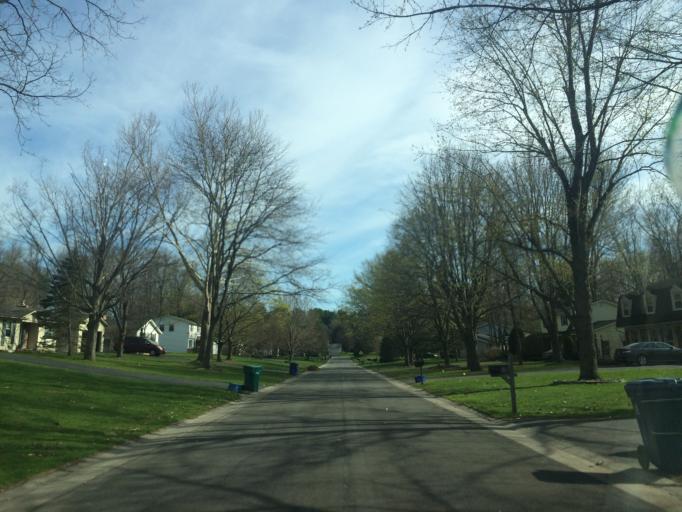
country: US
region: New York
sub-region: Monroe County
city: East Rochester
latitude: 43.0918
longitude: -77.4678
